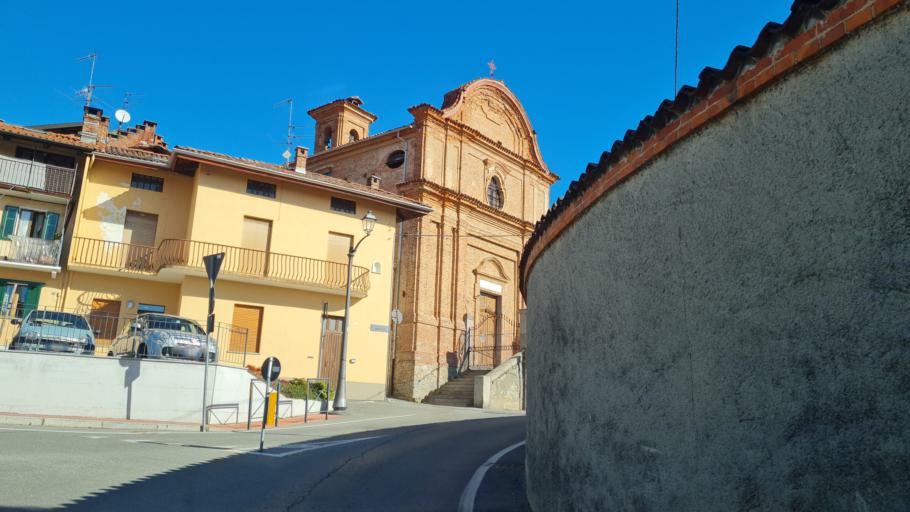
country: IT
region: Piedmont
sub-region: Provincia di Biella
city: Occhieppo Inferiore
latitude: 45.5535
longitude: 8.0230
